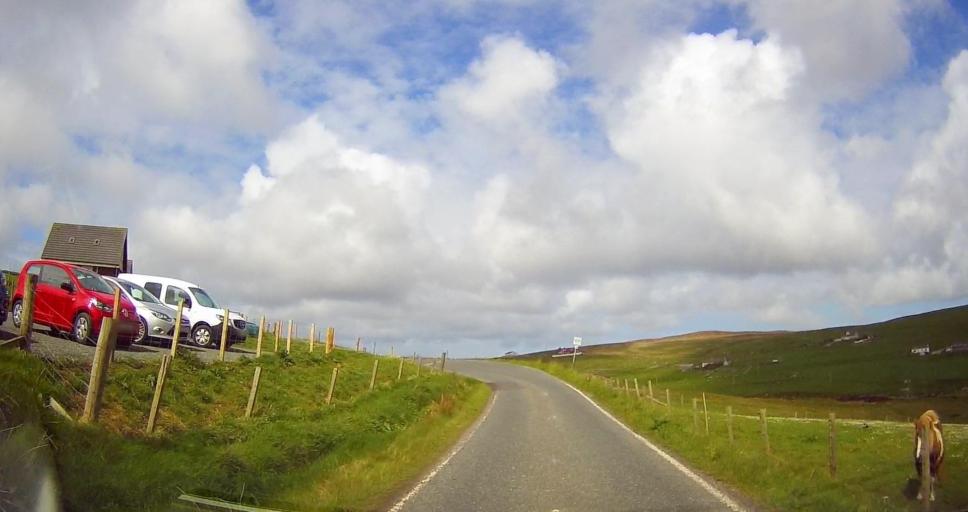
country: GB
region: Scotland
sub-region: Shetland Islands
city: Lerwick
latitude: 60.3024
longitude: -1.3470
